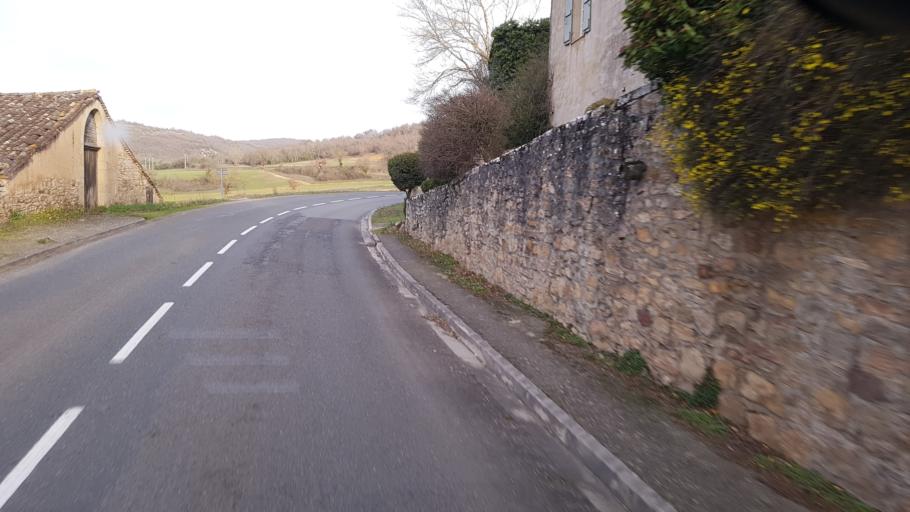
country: FR
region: Midi-Pyrenees
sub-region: Departement du Tarn-et-Garonne
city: Montricoux
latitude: 44.0110
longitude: 1.6823
